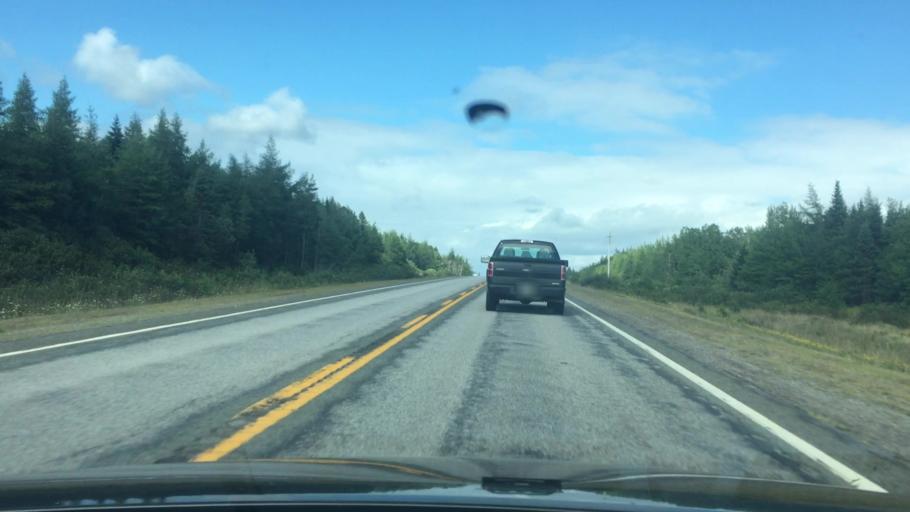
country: CA
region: Nova Scotia
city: Princeville
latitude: 45.6162
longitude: -61.0542
